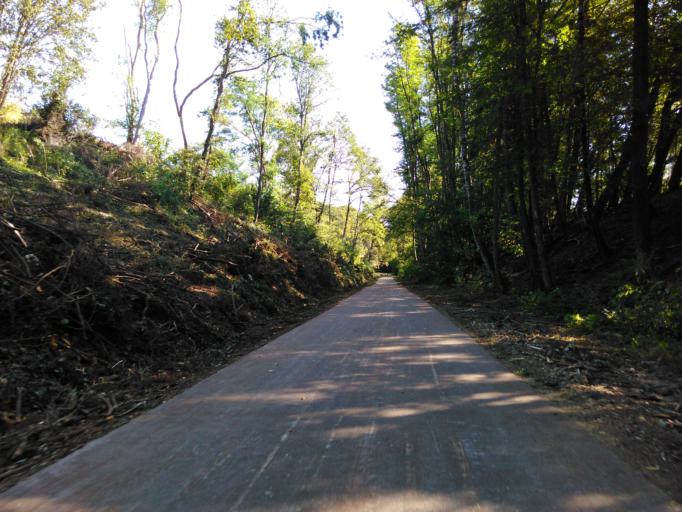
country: LU
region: Luxembourg
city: Eischen
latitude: 49.6895
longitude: 5.8903
